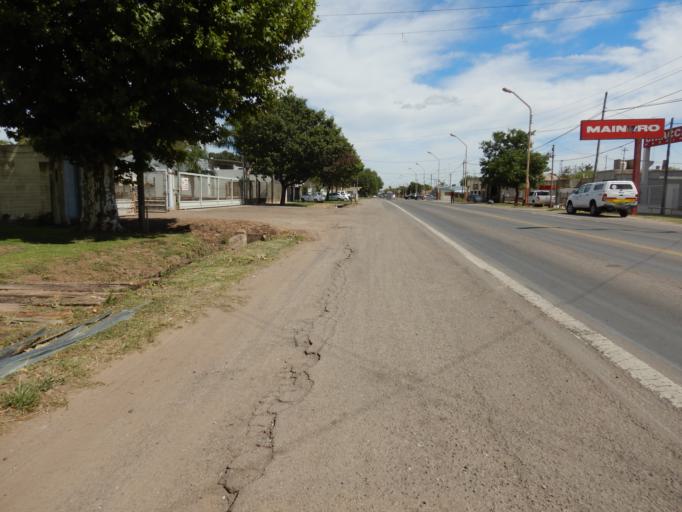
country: AR
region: Santa Fe
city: Carcarana
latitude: -32.8625
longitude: -61.1504
